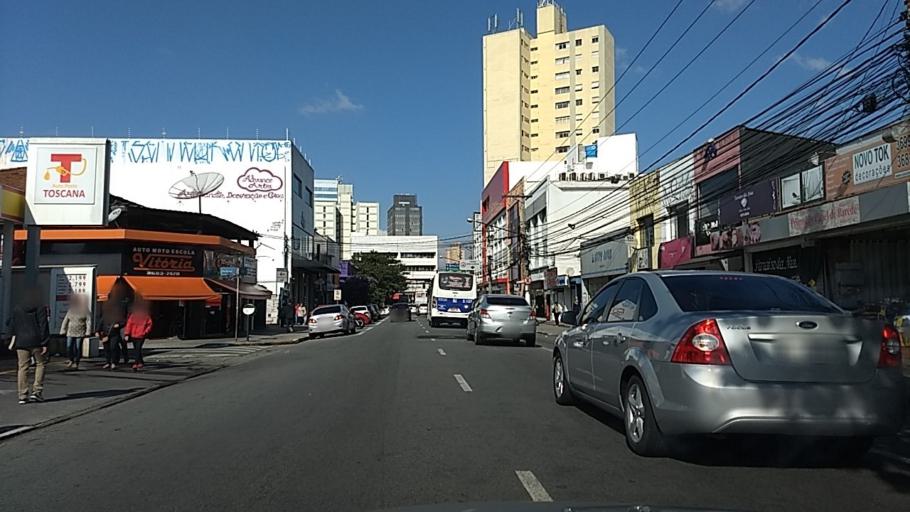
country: BR
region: Sao Paulo
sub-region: Osasco
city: Osasco
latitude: -23.5321
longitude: -46.7801
